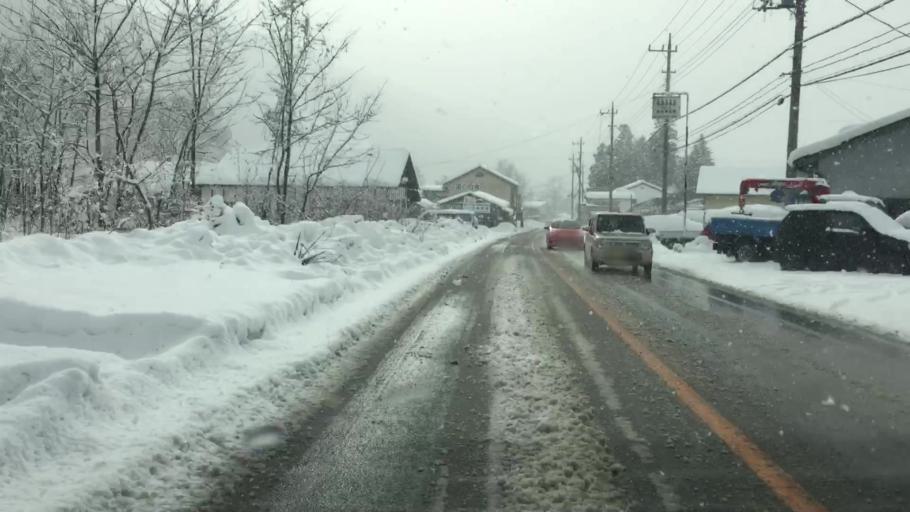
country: JP
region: Gunma
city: Numata
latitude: 36.7119
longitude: 139.0657
